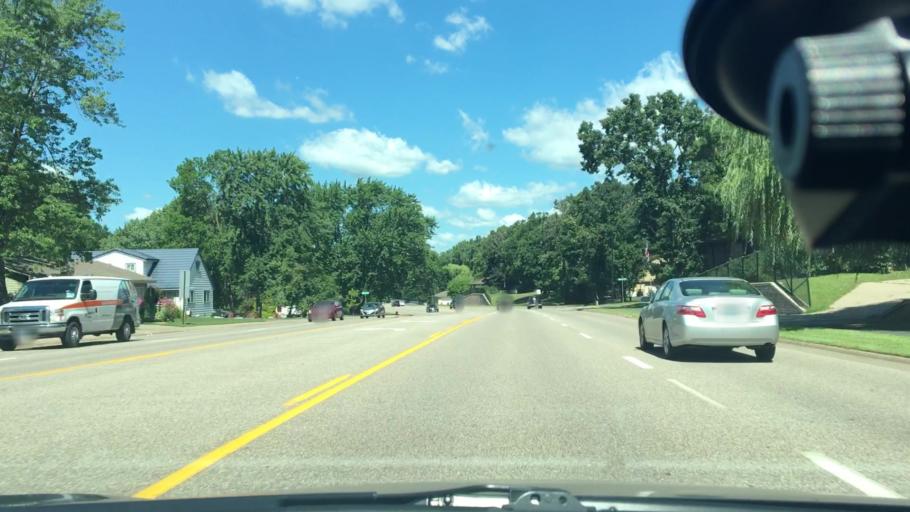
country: US
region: Minnesota
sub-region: Hennepin County
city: Maple Grove
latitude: 45.0709
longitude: -93.4531
